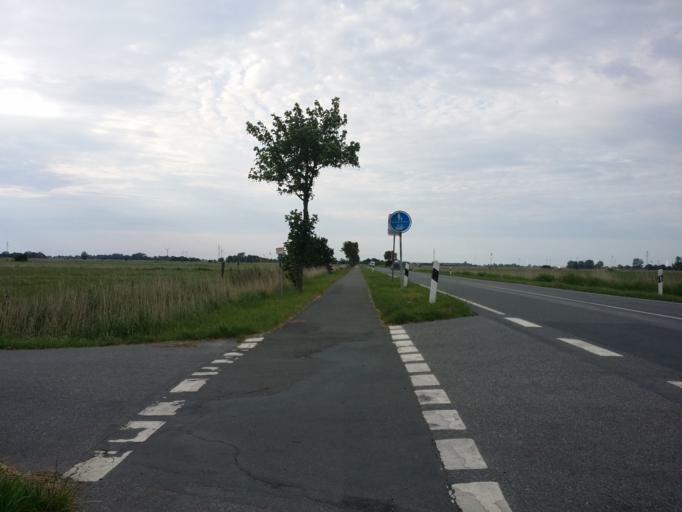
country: DE
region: Lower Saxony
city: Wittmund
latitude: 53.6069
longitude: 7.7957
